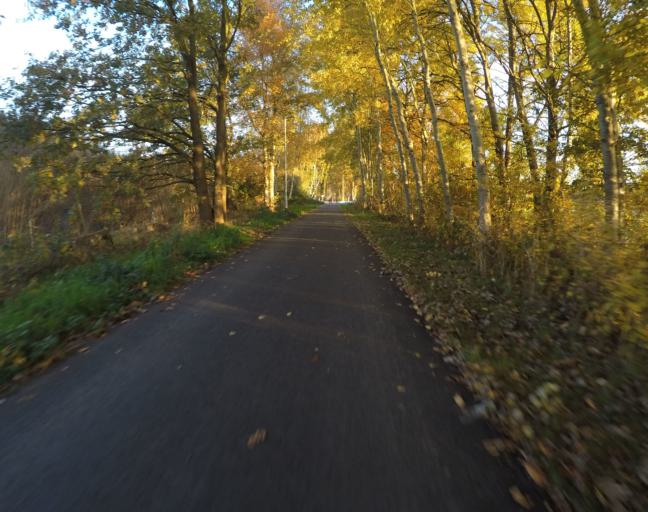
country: BE
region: Flanders
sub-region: Provincie Antwerpen
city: Hulshout
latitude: 51.0882
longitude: 4.8253
